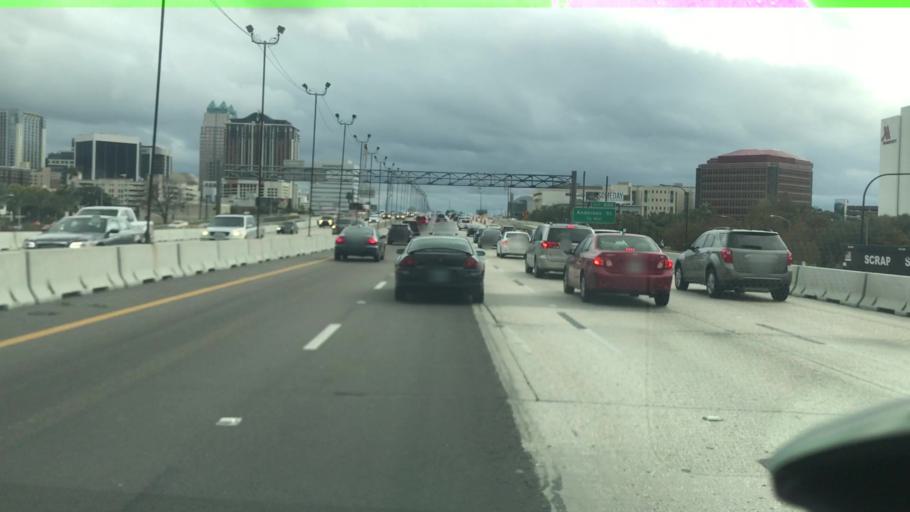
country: US
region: Florida
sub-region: Orange County
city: Orlando
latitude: 28.5492
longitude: -81.3826
